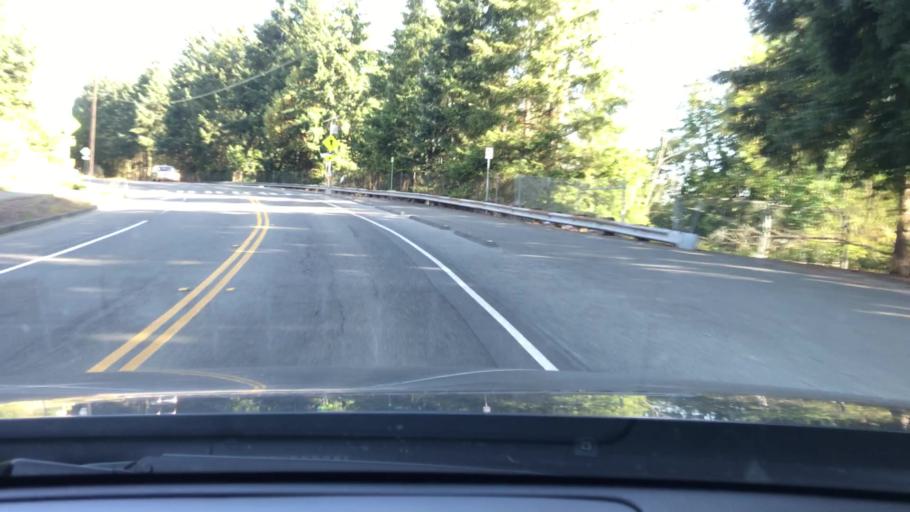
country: US
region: Washington
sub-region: King County
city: West Lake Sammamish
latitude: 47.5533
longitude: -122.0761
